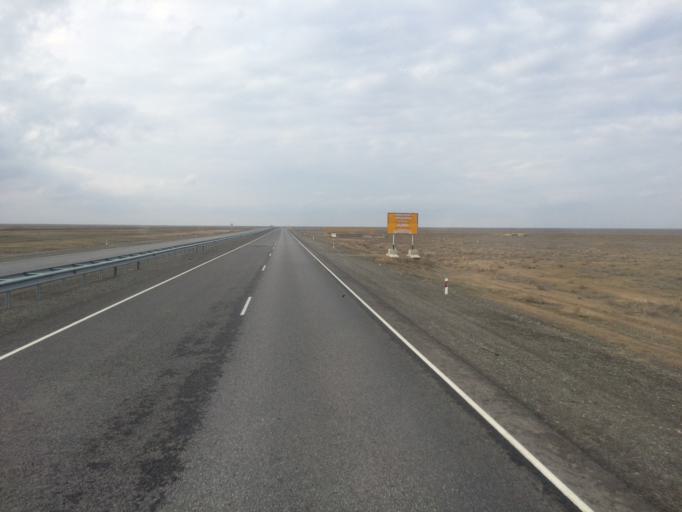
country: KZ
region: Ongtustik Qazaqstan
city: Turkestan
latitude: 43.5359
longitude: 67.7737
